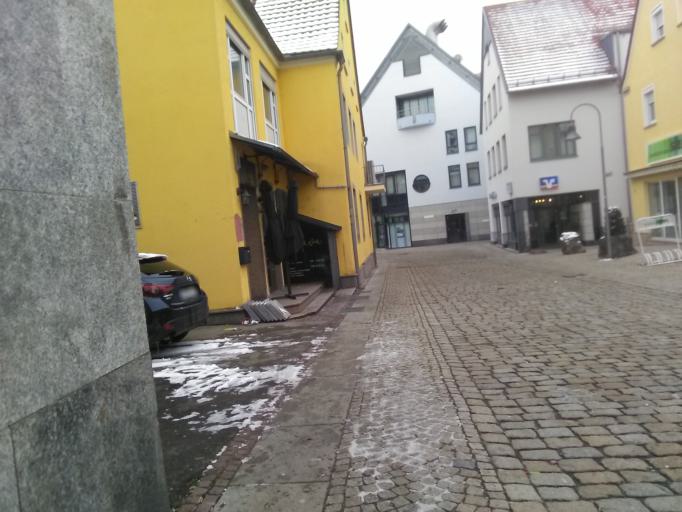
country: DE
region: Baden-Wuerttemberg
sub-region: Regierungsbezirk Stuttgart
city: Crailsheim
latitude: 49.1365
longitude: 10.0731
